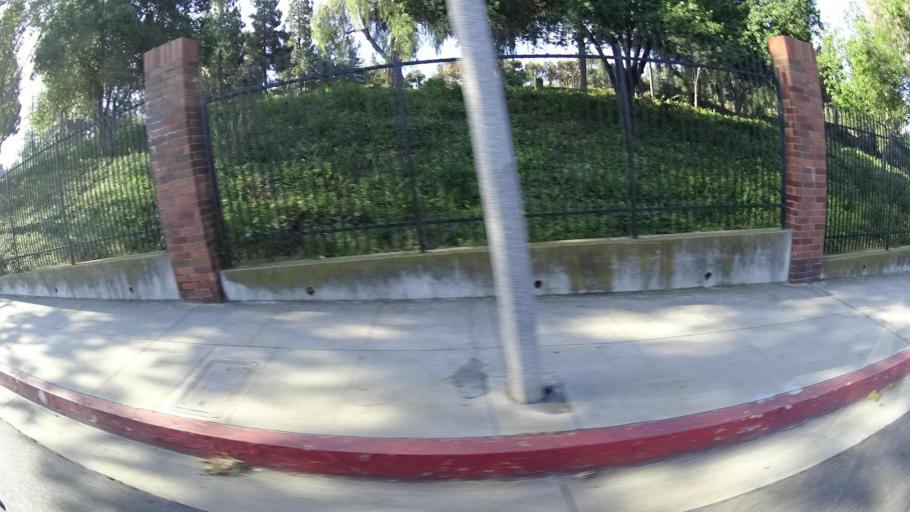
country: US
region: California
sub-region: Los Angeles County
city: La Puente
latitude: 34.0281
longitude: -117.9423
